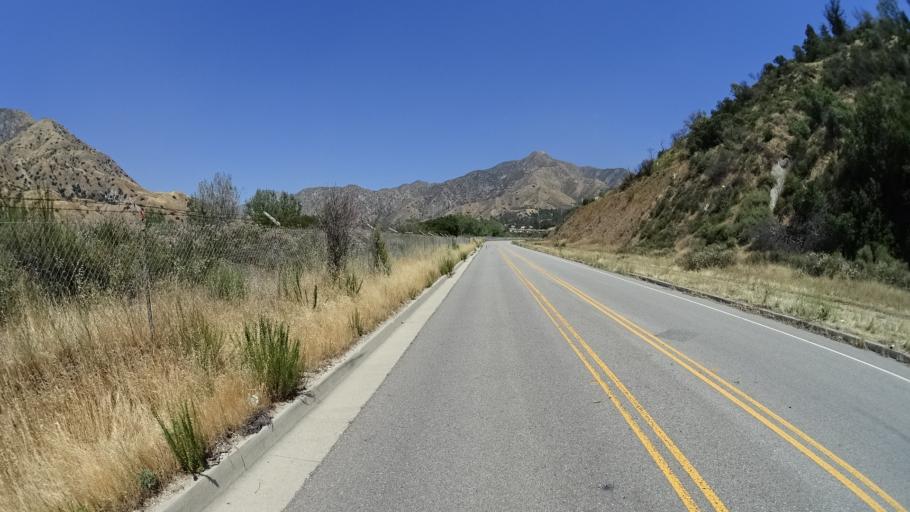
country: US
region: California
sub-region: Los Angeles County
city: La Crescenta-Montrose
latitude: 34.2767
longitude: -118.3066
